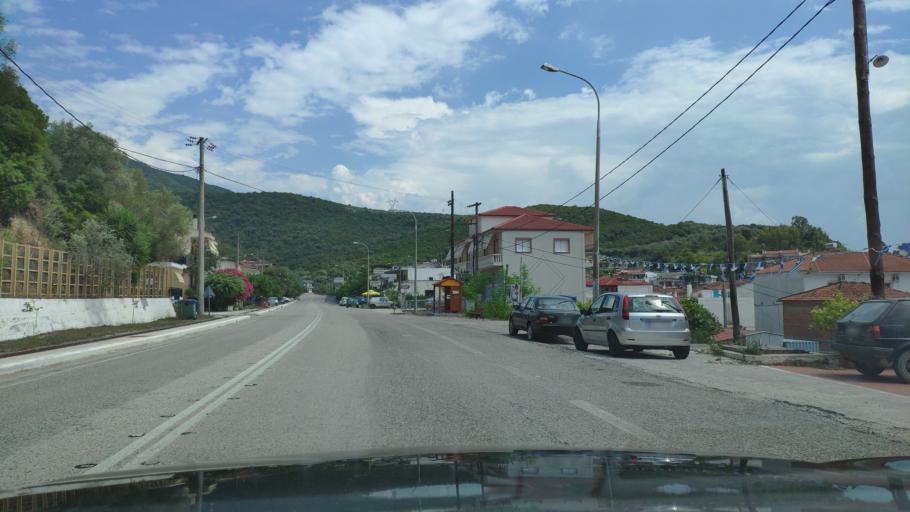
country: GR
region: West Greece
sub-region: Nomos Aitolias kai Akarnanias
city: Menidi
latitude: 39.0428
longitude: 21.1179
